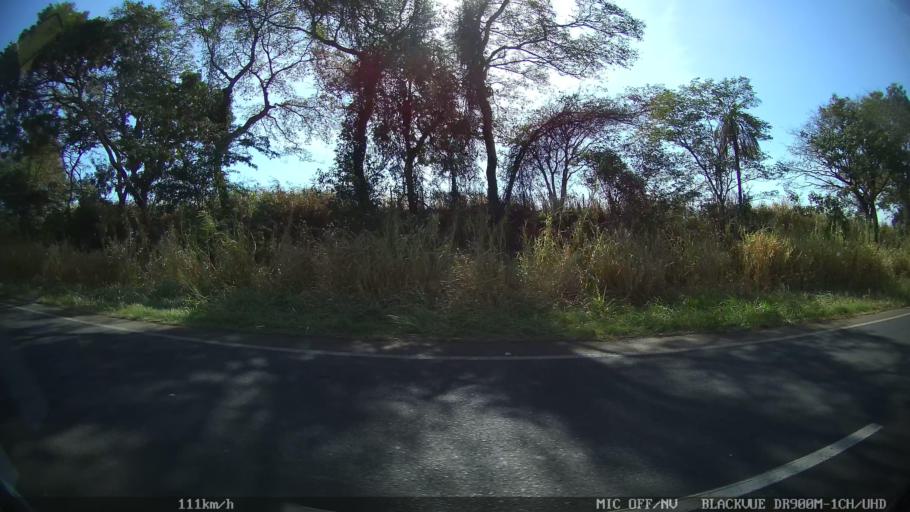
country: BR
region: Sao Paulo
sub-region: Barretos
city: Barretos
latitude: -20.5925
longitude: -48.7115
